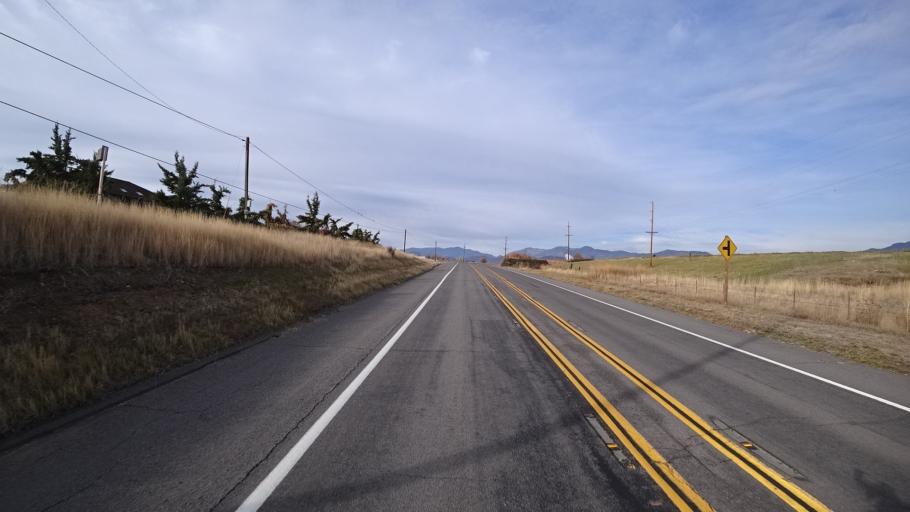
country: US
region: California
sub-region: Siskiyou County
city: Montague
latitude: 41.7289
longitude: -122.5676
